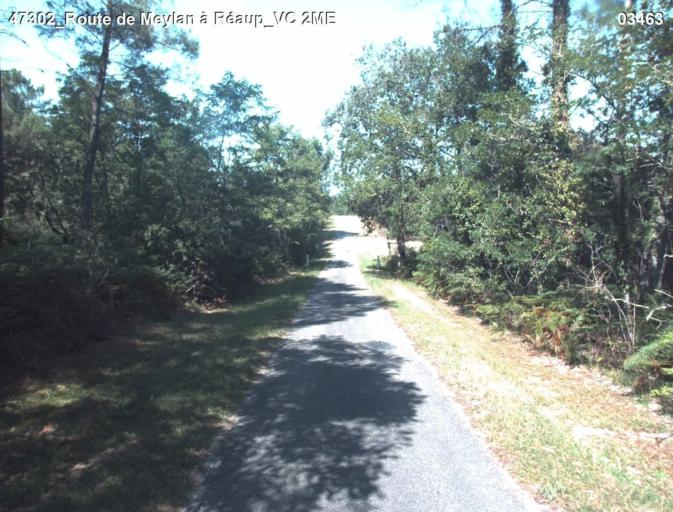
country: FR
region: Aquitaine
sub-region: Departement du Lot-et-Garonne
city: Mezin
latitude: 44.0794
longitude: 0.1242
